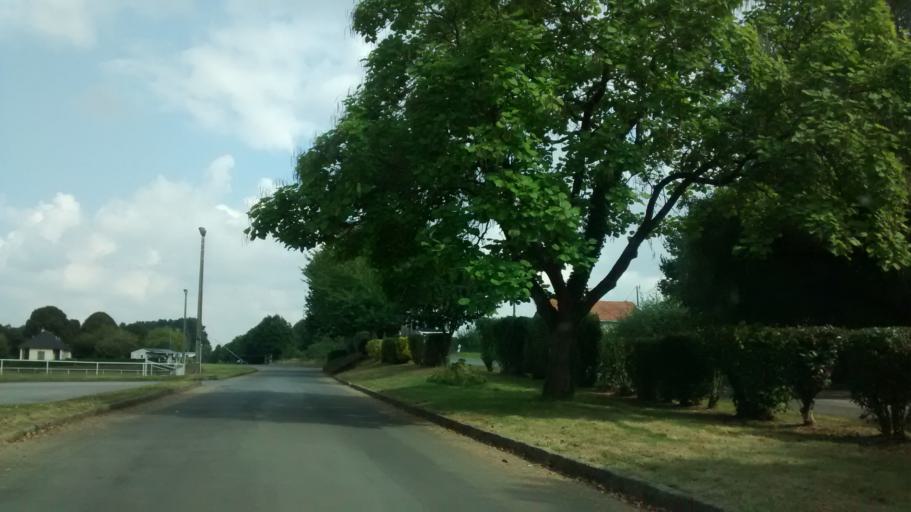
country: FR
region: Brittany
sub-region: Departement d'Ille-et-Vilaine
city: Chatillon-en-Vendelais
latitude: 48.2292
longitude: -1.1802
